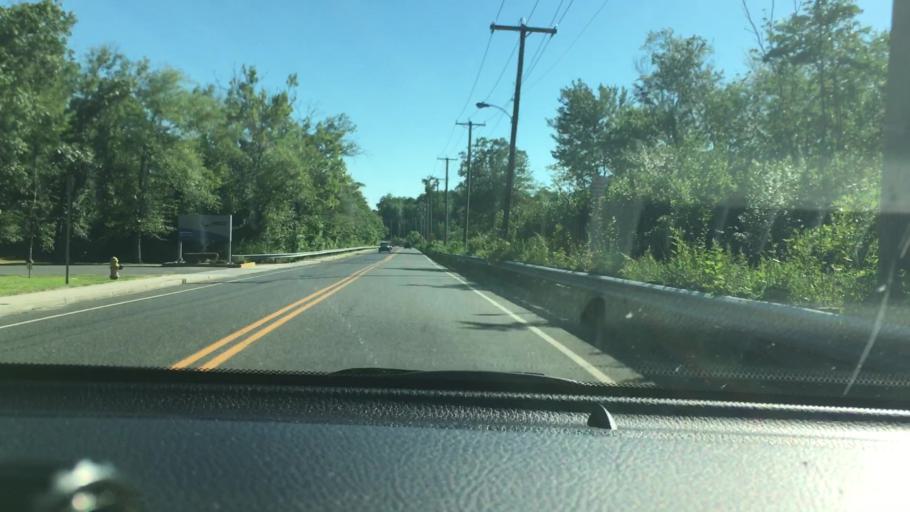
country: US
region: New Jersey
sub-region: Cumberland County
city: Millville
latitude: 39.4024
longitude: -75.0507
